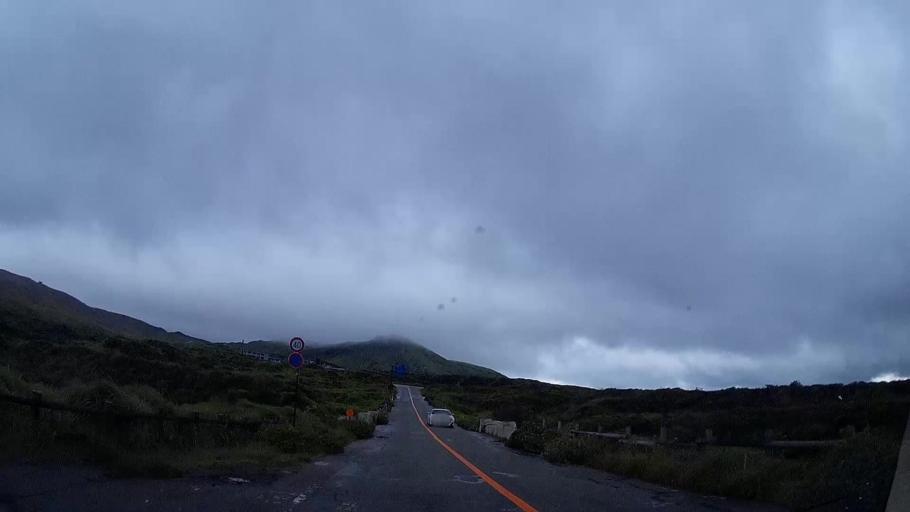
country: JP
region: Kumamoto
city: Aso
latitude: 32.8817
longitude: 131.0687
